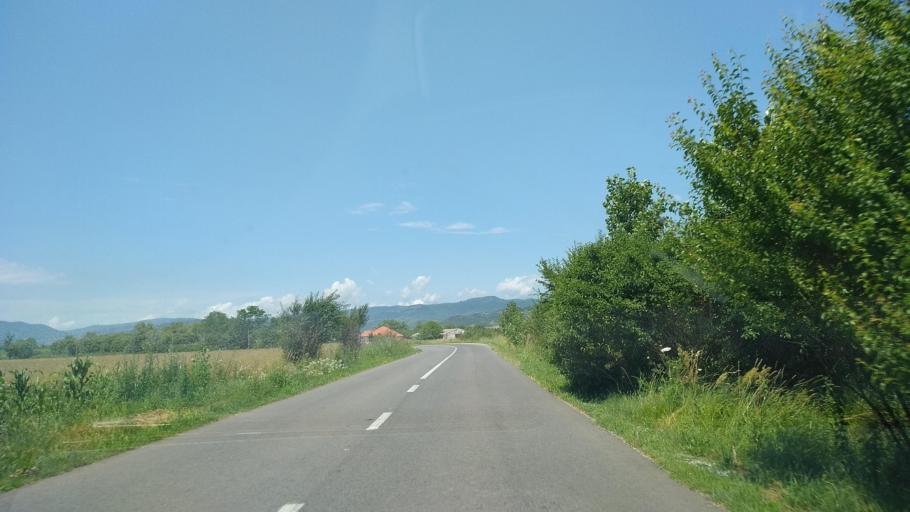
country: RO
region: Hunedoara
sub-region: Comuna Totesti
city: Totesti
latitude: 45.5765
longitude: 22.8593
